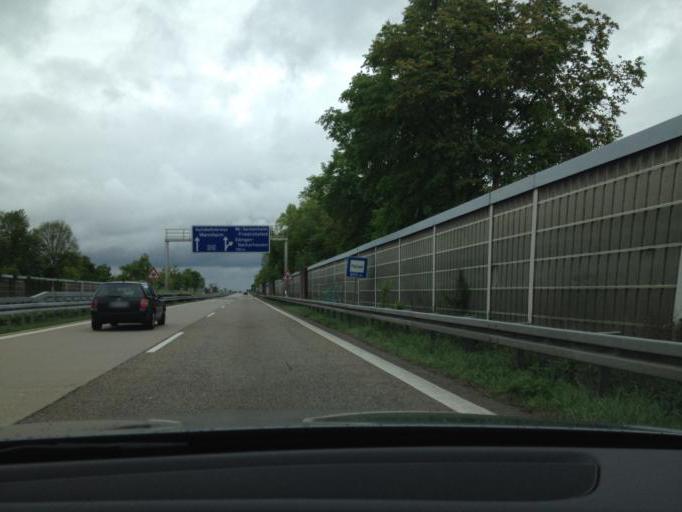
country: DE
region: Baden-Wuerttemberg
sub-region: Karlsruhe Region
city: Edingen-Neckarhausen
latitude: 49.4448
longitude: 8.5840
